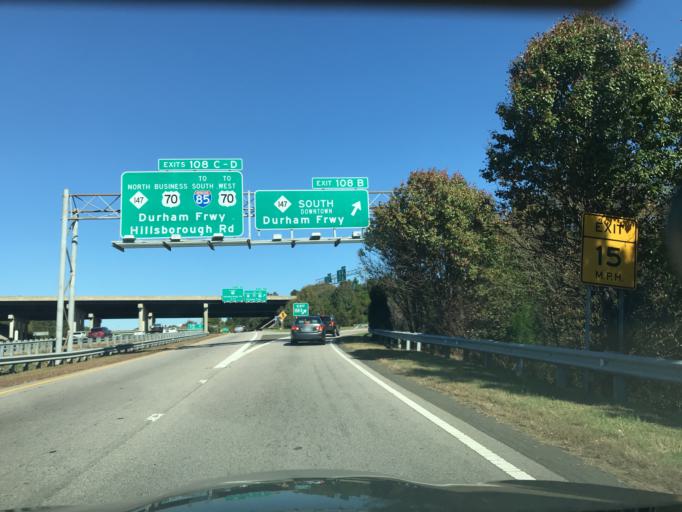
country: US
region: North Carolina
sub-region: Durham County
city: Durham
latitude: 36.0150
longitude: -78.9520
